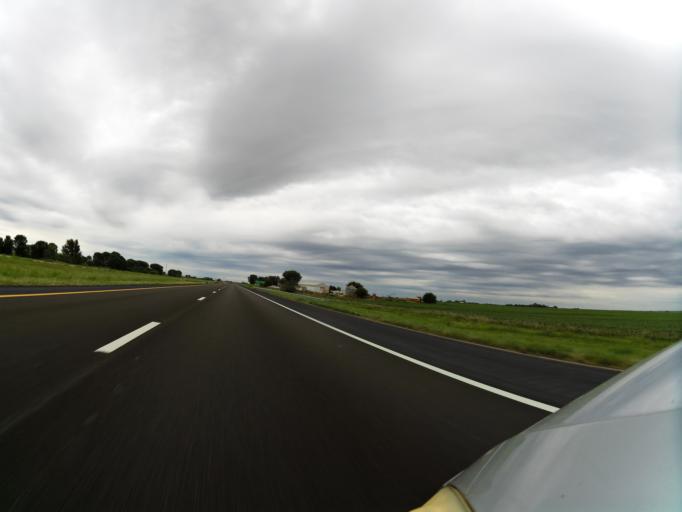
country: US
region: Kansas
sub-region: Sedgwick County
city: Colwich
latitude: 37.8487
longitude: -97.5955
